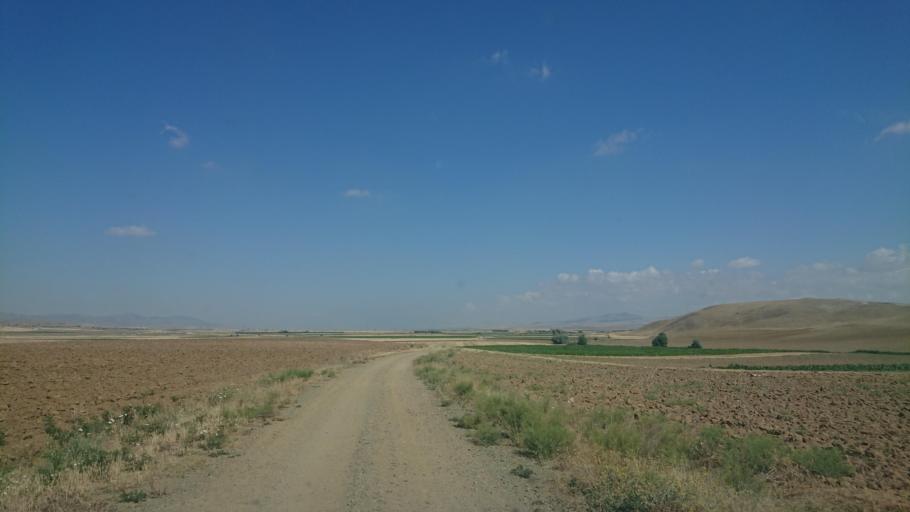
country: TR
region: Aksaray
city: Sariyahsi
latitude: 38.9682
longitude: 33.9209
